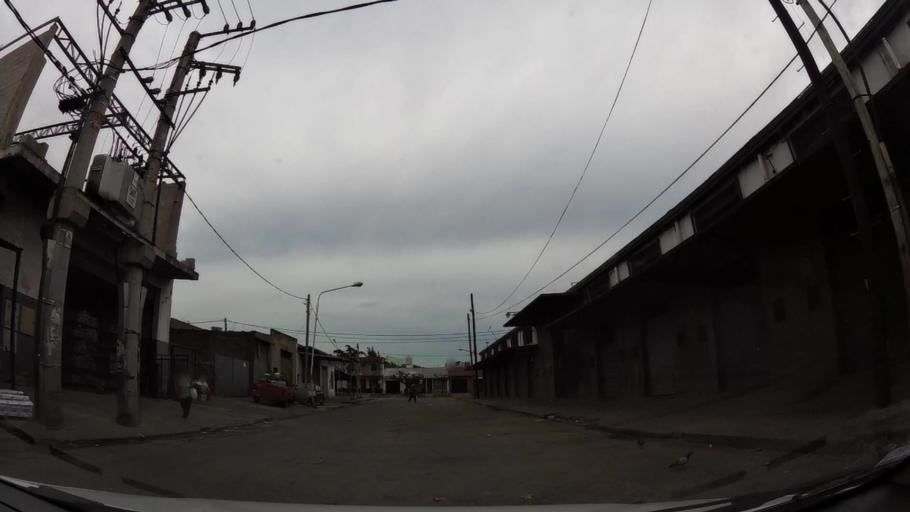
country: AR
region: Buenos Aires
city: San Justo
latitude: -34.6650
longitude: -58.5200
